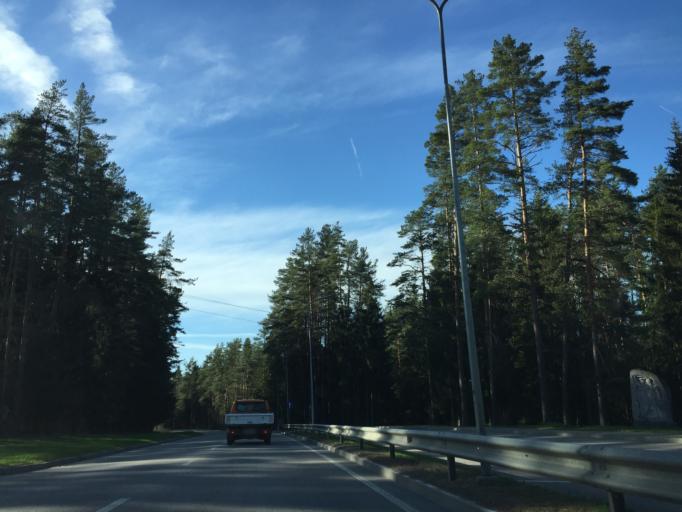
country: LV
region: Valkas Rajons
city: Valka
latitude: 57.7836
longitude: 26.0027
